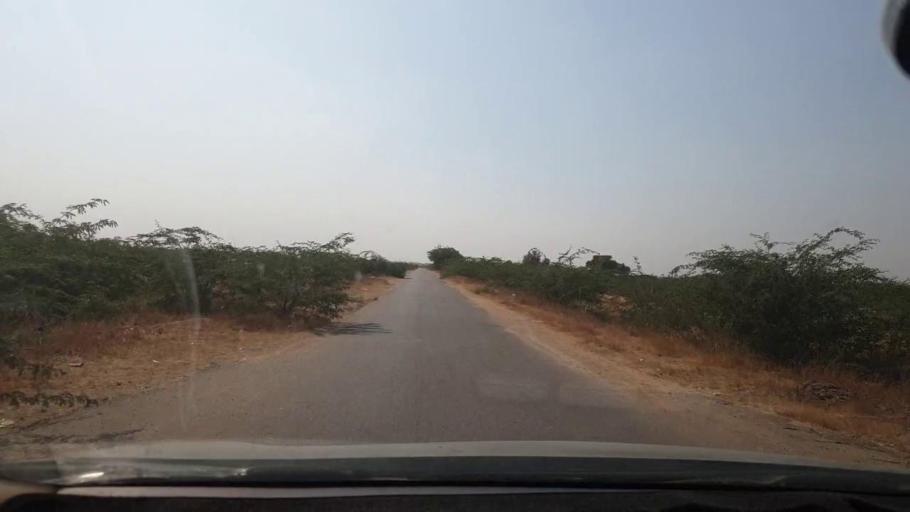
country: PK
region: Sindh
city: Malir Cantonment
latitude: 25.1271
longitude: 67.2249
